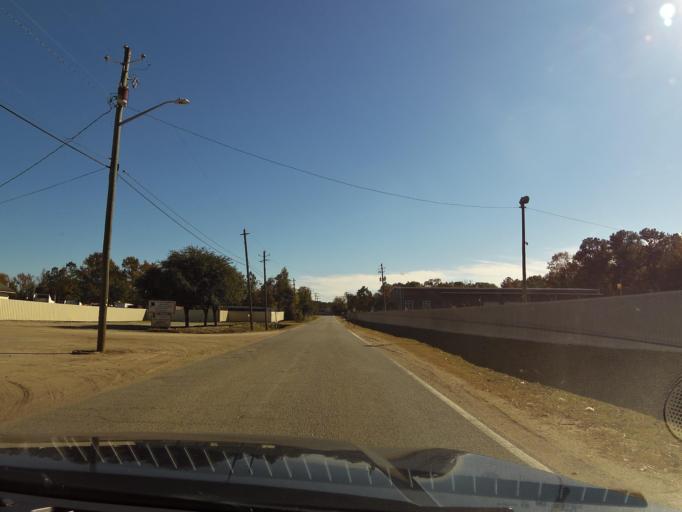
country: US
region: Georgia
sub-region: Chatham County
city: Savannah
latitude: 32.0600
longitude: -81.1350
